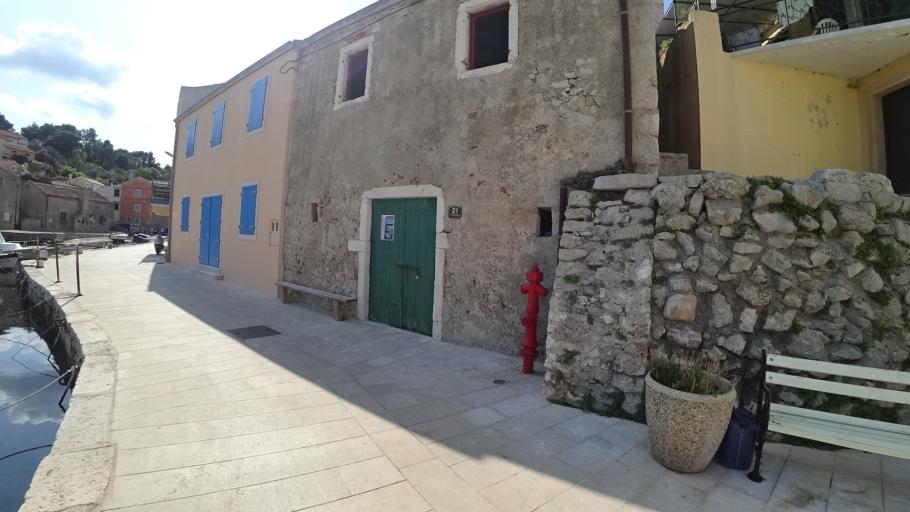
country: HR
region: Primorsko-Goranska
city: Mali Losinj
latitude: 44.5198
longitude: 14.5052
